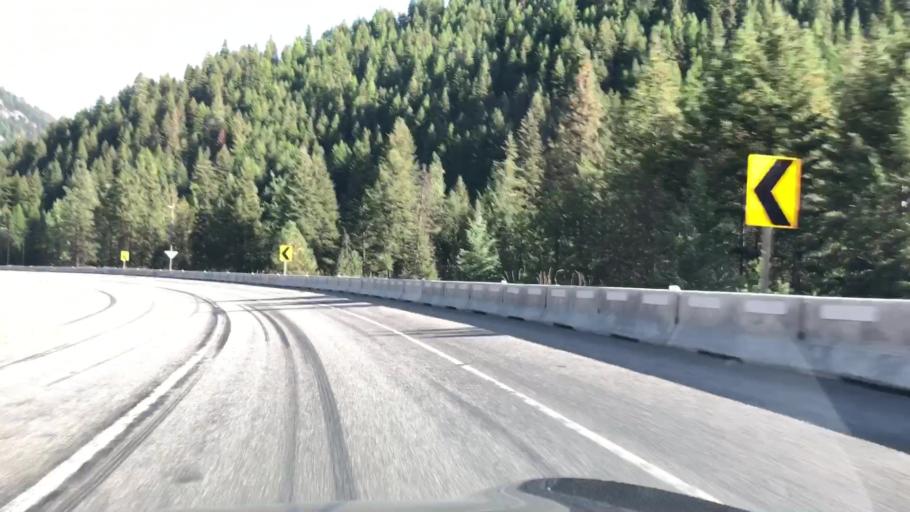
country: US
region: Montana
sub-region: Sanders County
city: Thompson Falls
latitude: 47.3322
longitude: -115.2656
